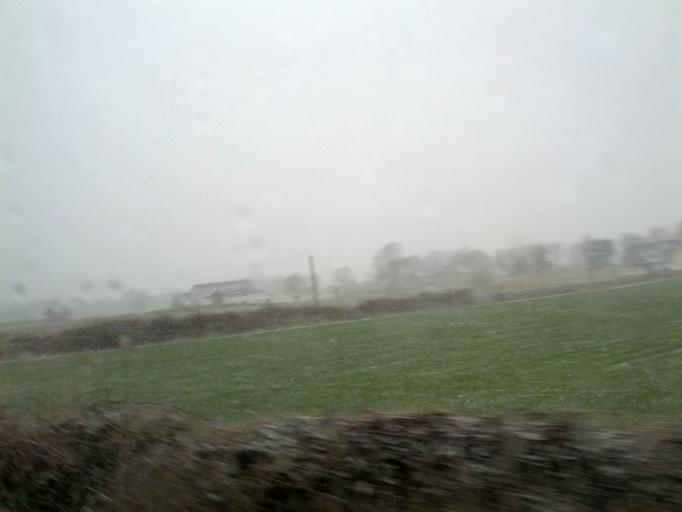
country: IE
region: Connaught
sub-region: County Galway
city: Oranmore
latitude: 53.2047
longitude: -8.8916
